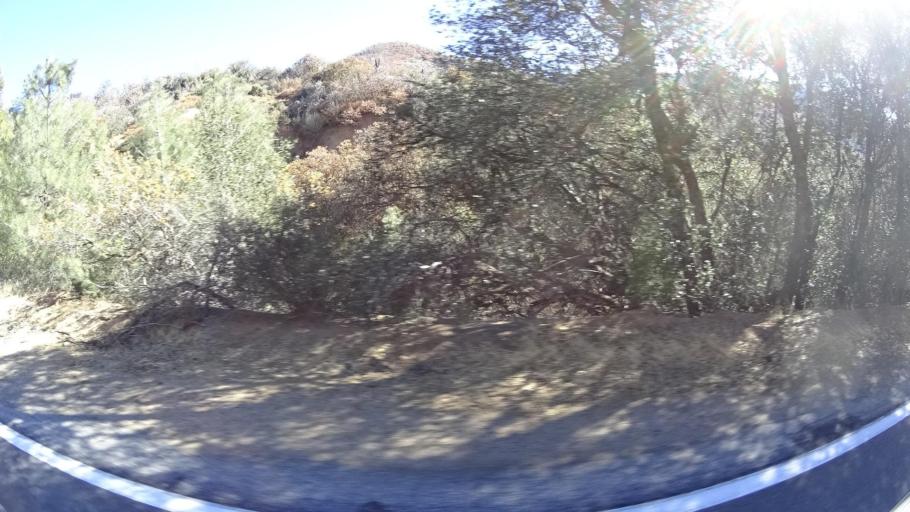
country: US
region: California
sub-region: Kern County
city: Alta Sierra
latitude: 35.7474
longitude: -118.5876
